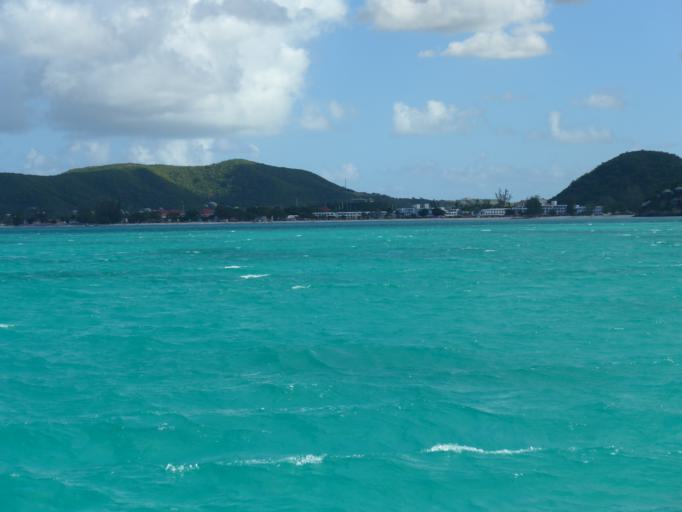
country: AG
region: Saint Mary
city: Bolands
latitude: 17.0553
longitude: -61.9005
